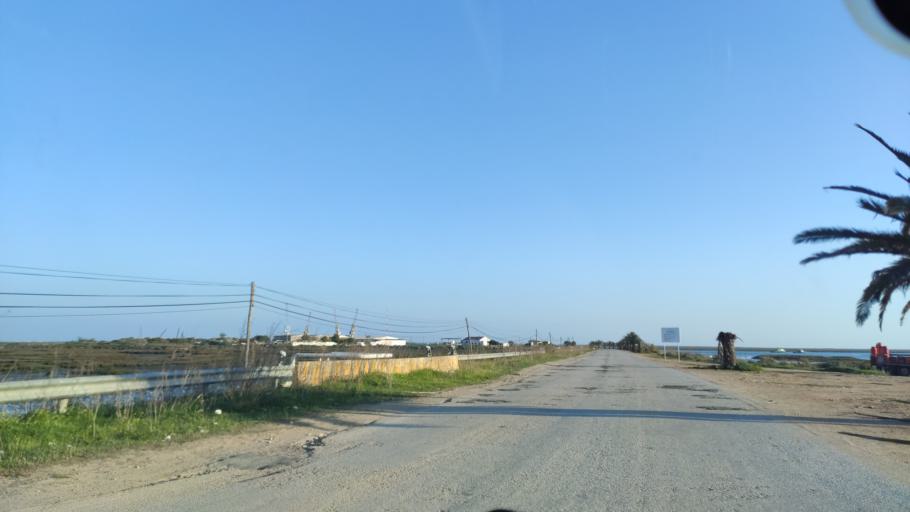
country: PT
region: Faro
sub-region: Faro
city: Faro
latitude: 37.0080
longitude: -7.9253
